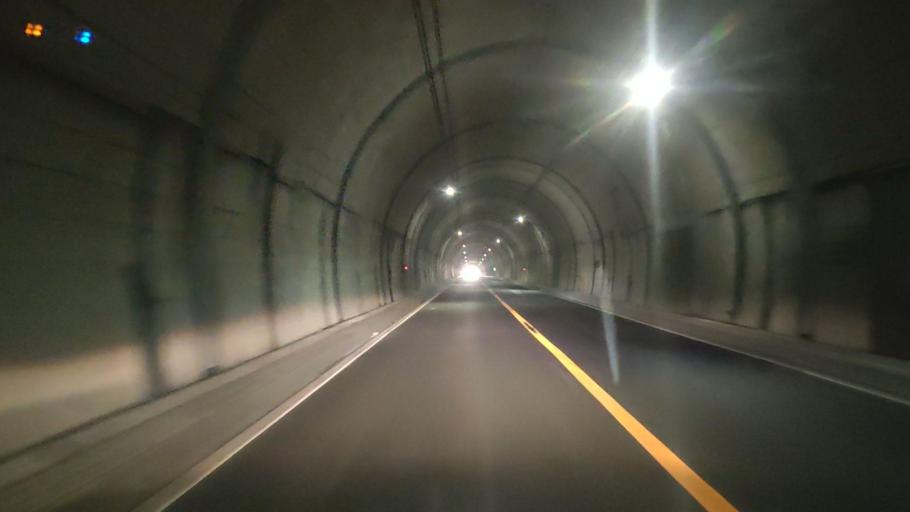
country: JP
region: Oita
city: Saiki
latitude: 32.8819
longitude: 131.9472
